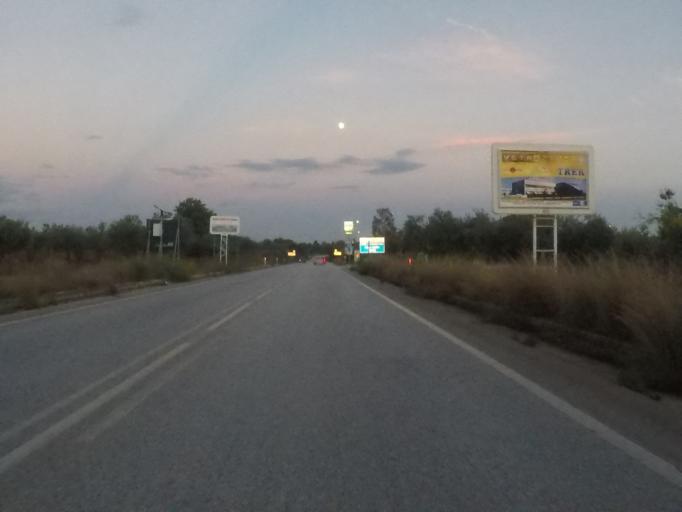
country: IT
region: Sicily
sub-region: Trapani
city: Castelvetrano
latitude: 37.6578
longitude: 12.8163
